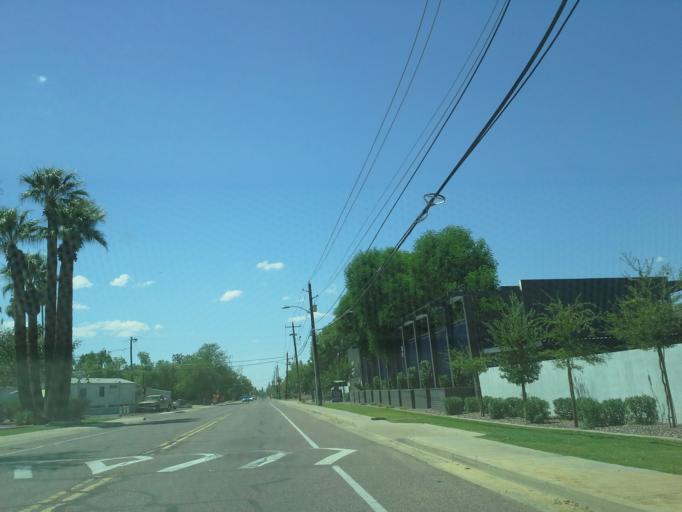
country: US
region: Arizona
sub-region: Maricopa County
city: Phoenix
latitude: 33.5056
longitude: -112.0501
